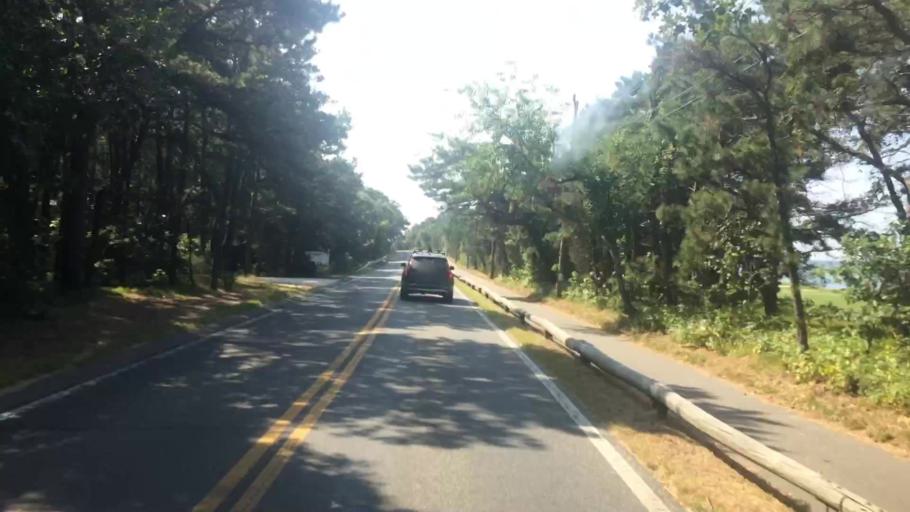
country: US
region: Massachusetts
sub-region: Dukes County
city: Oak Bluffs
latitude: 41.4373
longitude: -70.5571
